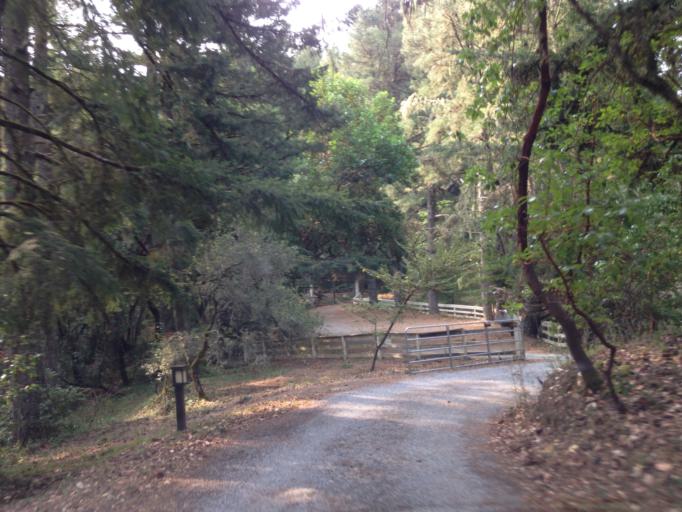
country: US
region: California
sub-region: San Mateo County
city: Portola Valley
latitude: 37.3791
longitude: -122.2954
